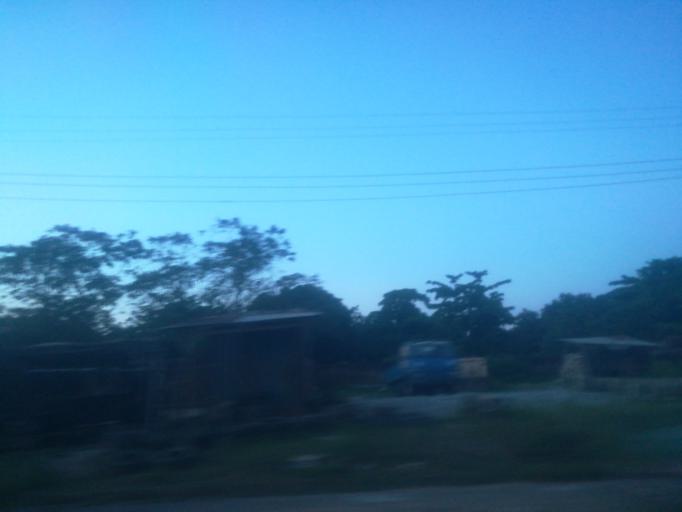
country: NG
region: Ogun
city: Abeokuta
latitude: 7.1865
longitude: 3.4334
